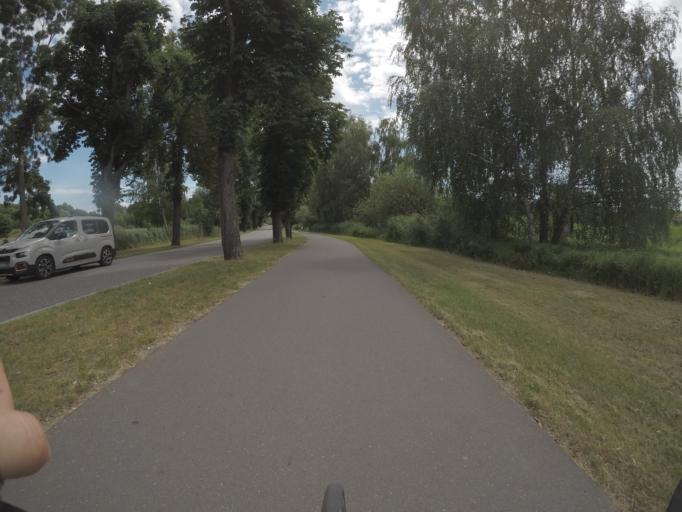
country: DE
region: Brandenburg
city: Storkow
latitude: 52.2517
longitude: 13.9370
